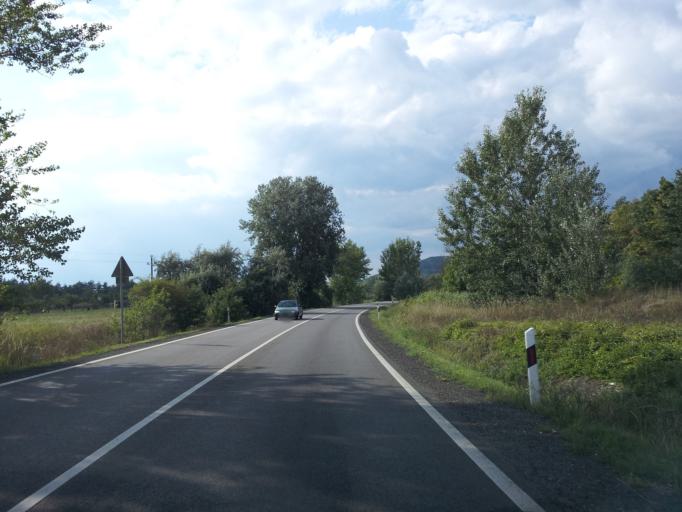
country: HU
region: Pest
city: Vac
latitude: 47.8051
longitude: 19.0976
